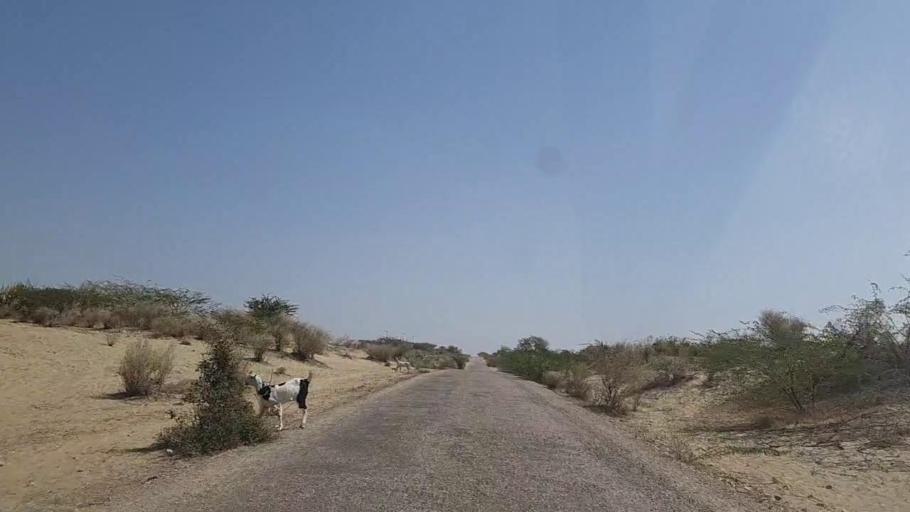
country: PK
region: Sindh
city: Diplo
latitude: 24.5142
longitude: 69.3850
